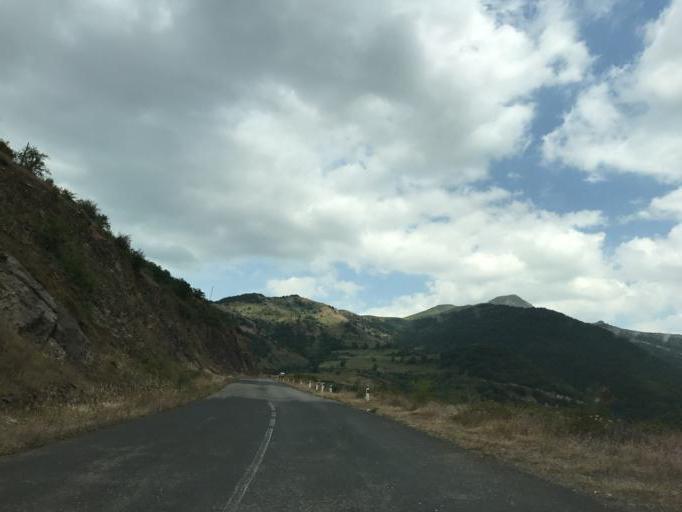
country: AZ
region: Lacin
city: Lacin
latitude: 39.6779
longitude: 46.6299
